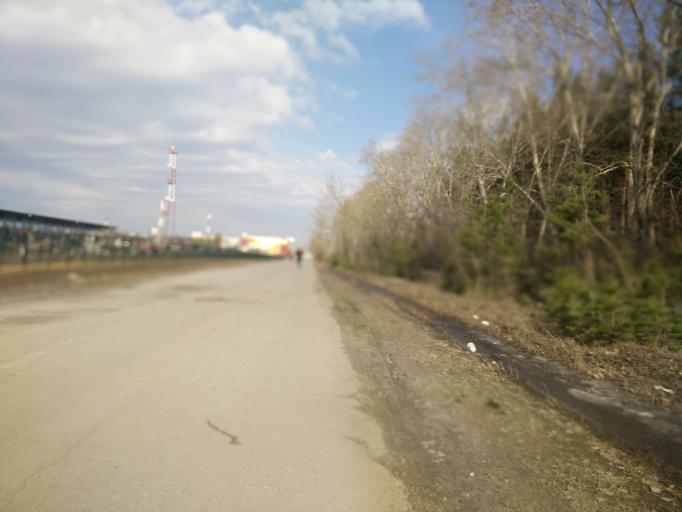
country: RU
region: Novosibirsk
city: Berdsk
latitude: 54.7618
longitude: 83.0734
